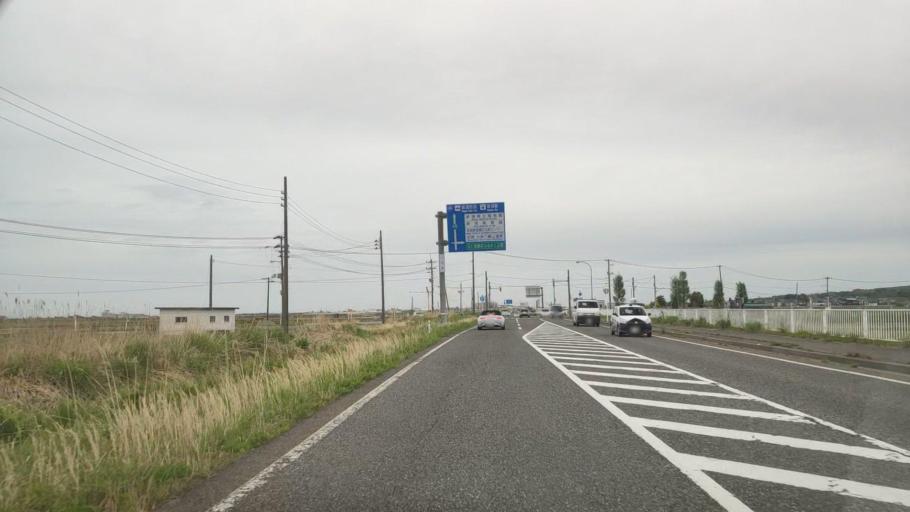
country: JP
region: Niigata
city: Niitsu-honcho
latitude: 37.7701
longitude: 139.1020
